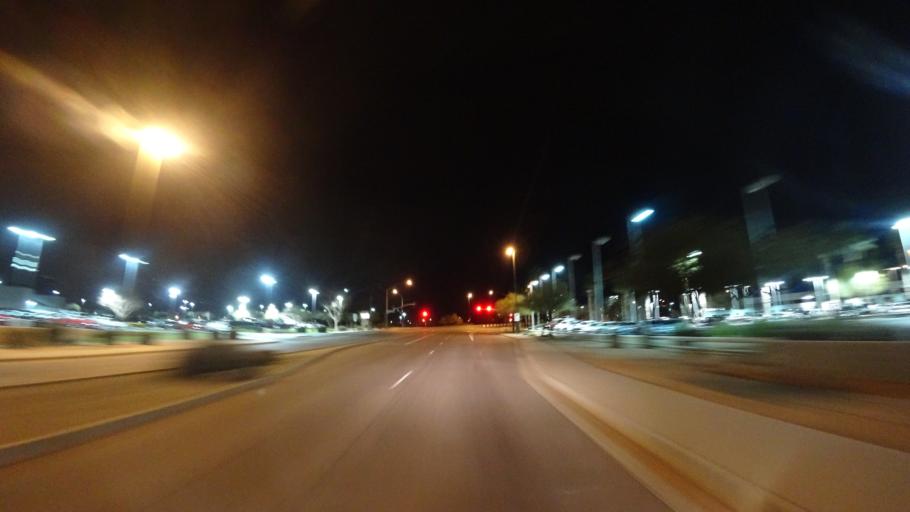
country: US
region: Arizona
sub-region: Maricopa County
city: Gilbert
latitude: 33.3894
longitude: -111.6953
